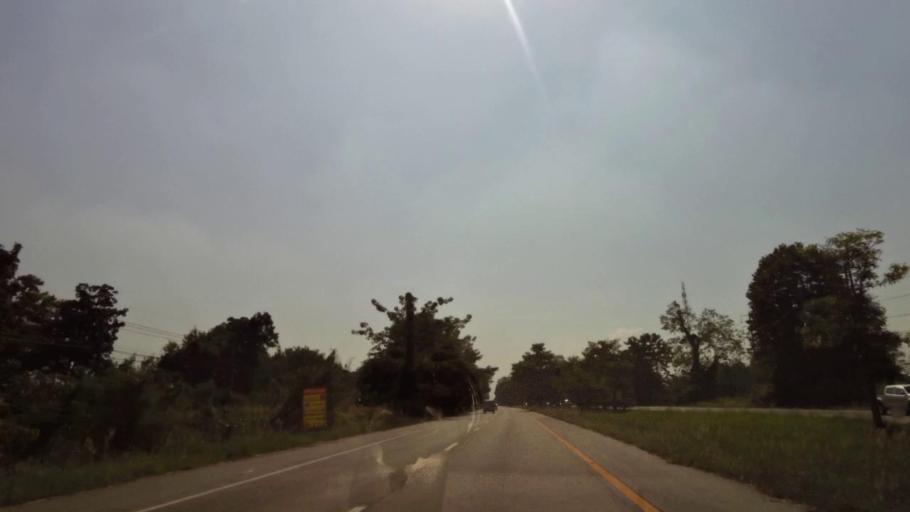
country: TH
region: Phichit
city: Wachira Barami
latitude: 16.6382
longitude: 100.1496
